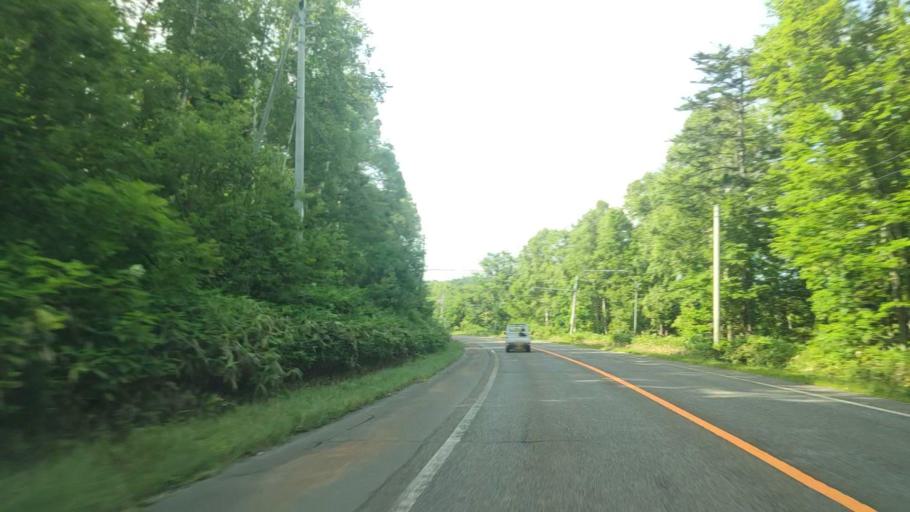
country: JP
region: Hokkaido
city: Nayoro
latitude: 44.3901
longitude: 142.3975
